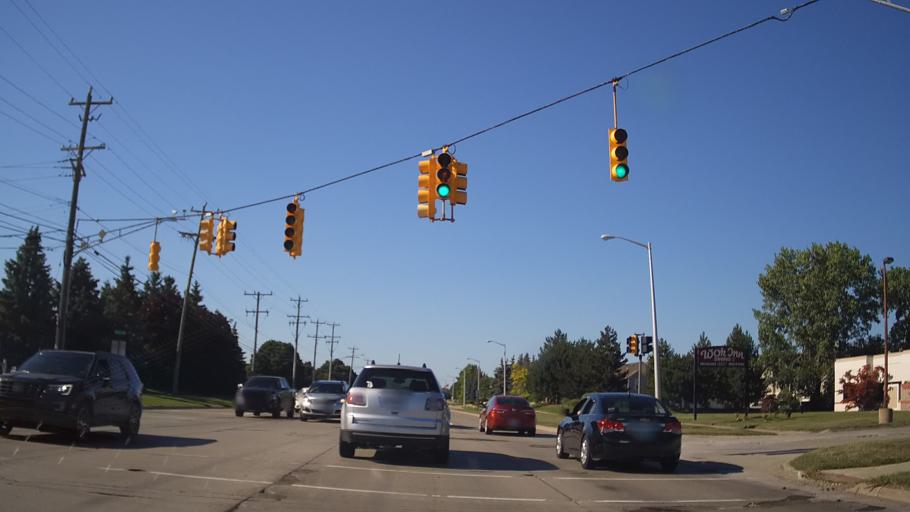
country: US
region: Michigan
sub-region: Macomb County
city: Utica
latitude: 42.6196
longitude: -82.9730
